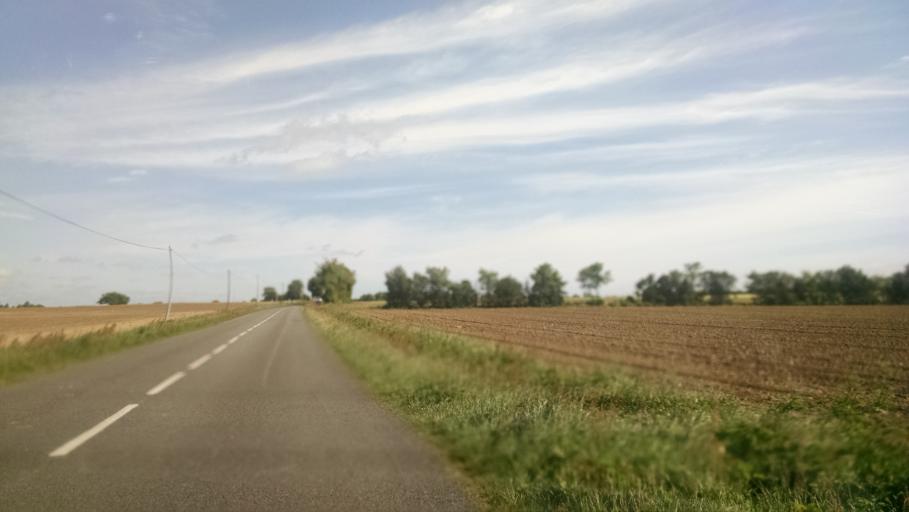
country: FR
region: Pays de la Loire
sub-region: Departement de la Loire-Atlantique
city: Saint-Hilaire-de-Clisson
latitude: 47.0425
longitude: -1.3242
